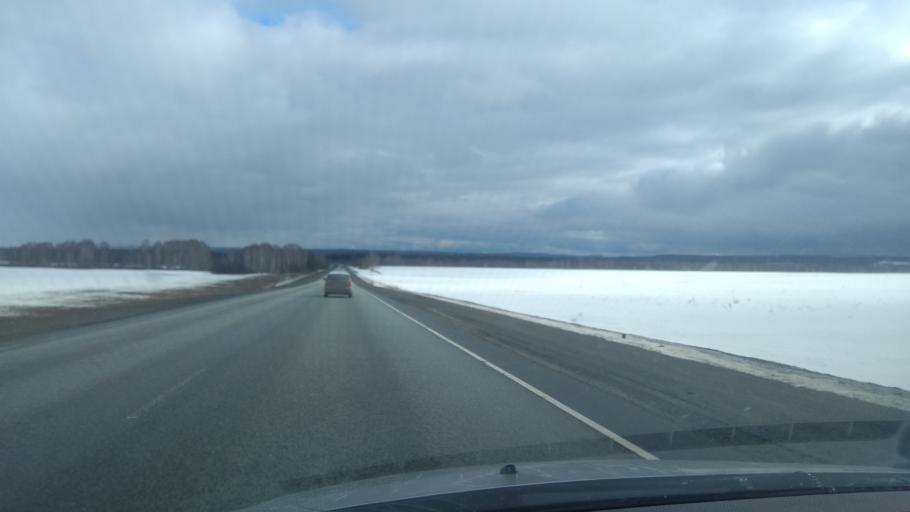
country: RU
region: Sverdlovsk
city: Ufimskiy
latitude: 56.7729
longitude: 58.0681
